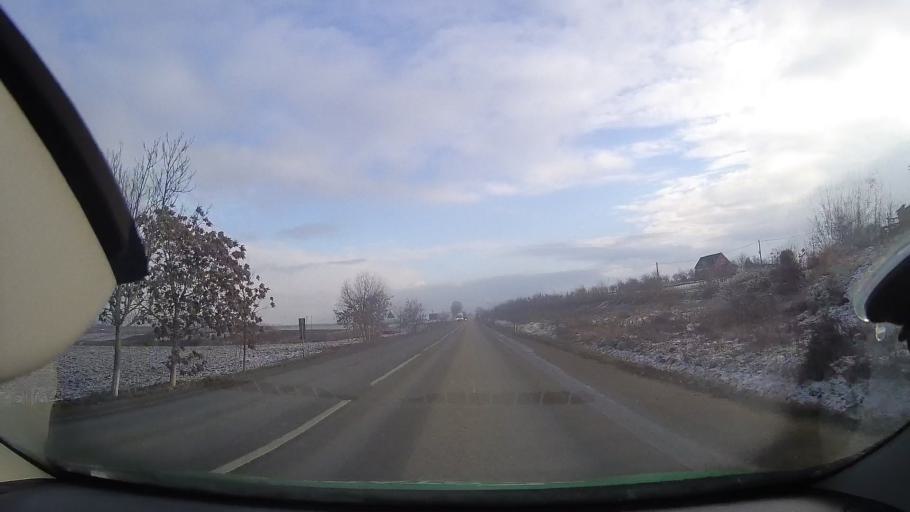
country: RO
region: Mures
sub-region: Comuna Cuci
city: Cuci
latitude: 46.4608
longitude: 24.1644
